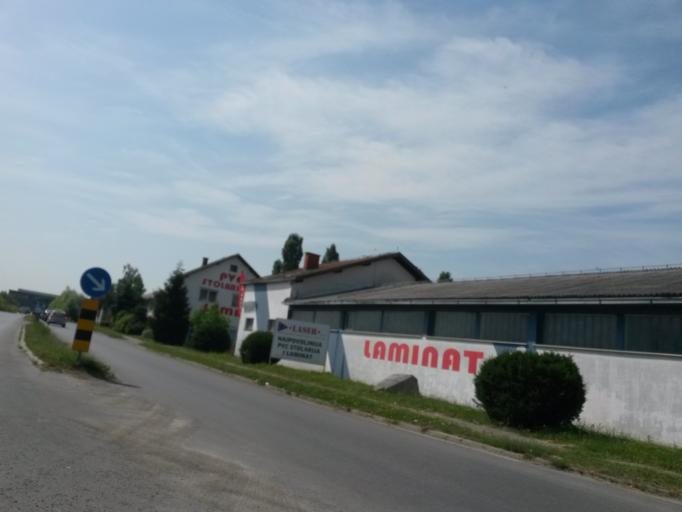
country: HR
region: Osjecko-Baranjska
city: Brijest
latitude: 45.5408
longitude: 18.6482
